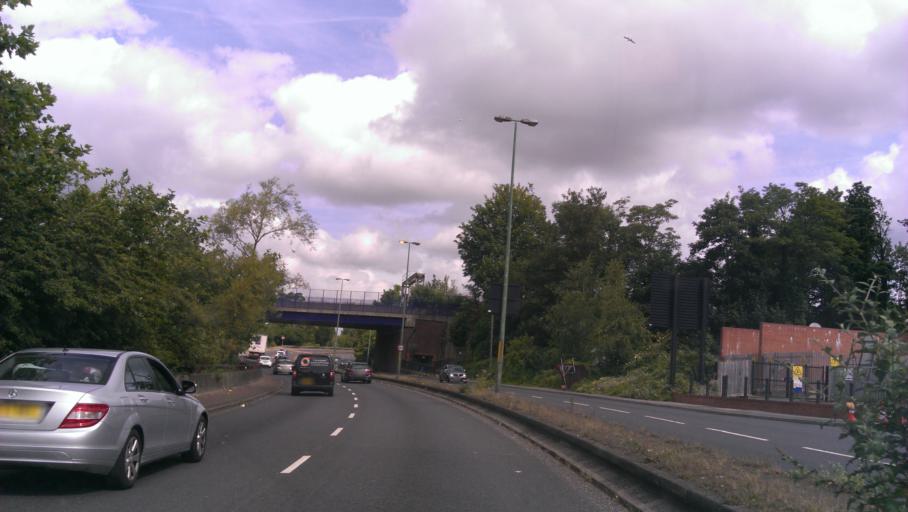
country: GB
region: England
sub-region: Kent
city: Maidstone
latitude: 51.2762
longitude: 0.5184
